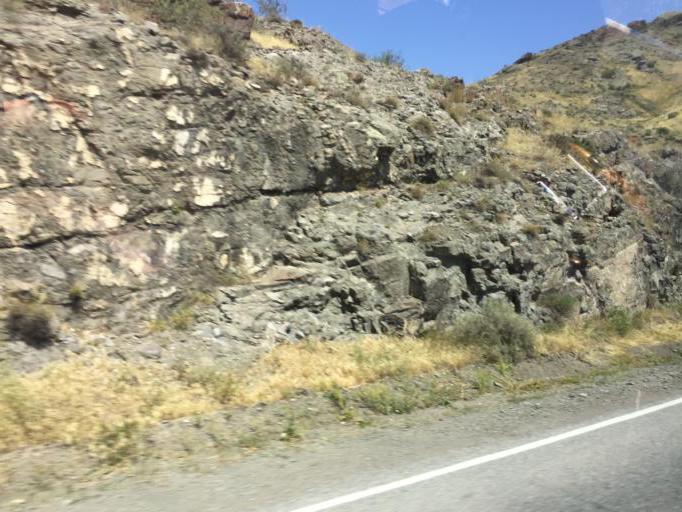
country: AM
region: Vayots' Dzori Marz
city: Zarrit'ap'
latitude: 39.7150
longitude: 45.6184
